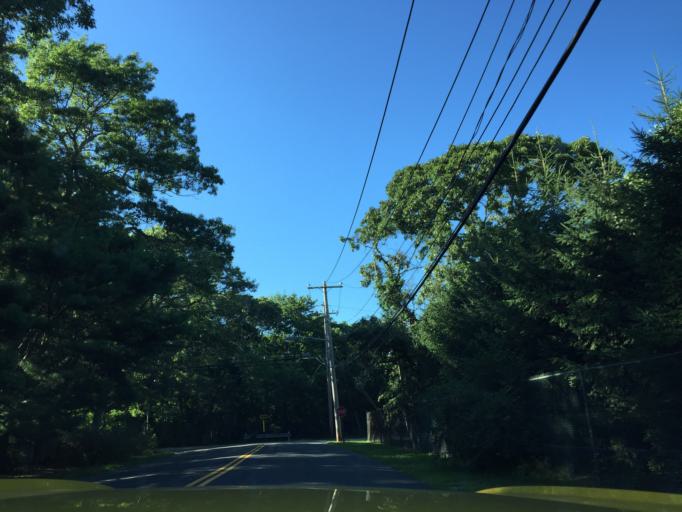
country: US
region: New York
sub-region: Suffolk County
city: Southold
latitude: 41.0551
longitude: -72.4192
